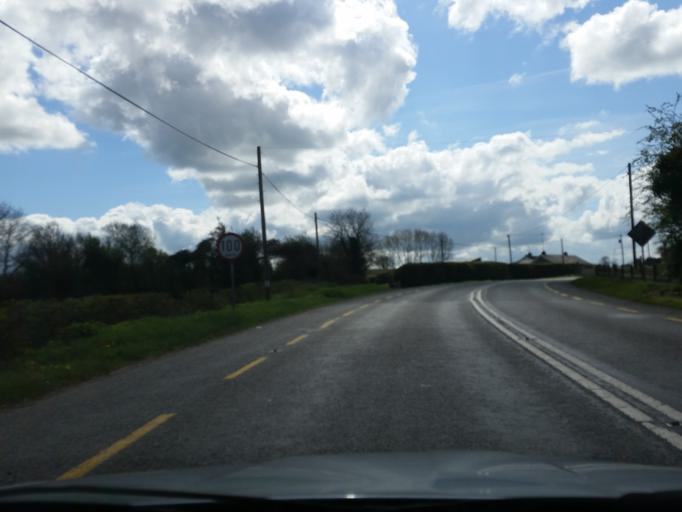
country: IE
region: Leinster
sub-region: An Mhi
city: Slane
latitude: 53.6945
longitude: -6.5387
